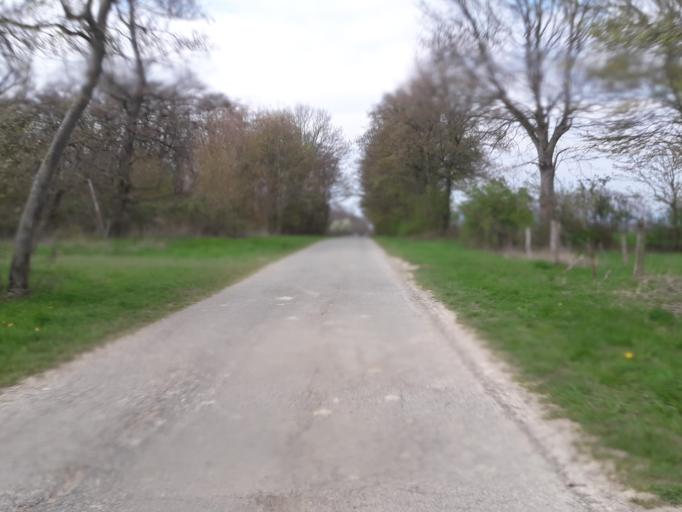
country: DE
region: North Rhine-Westphalia
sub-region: Regierungsbezirk Detmold
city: Paderborn
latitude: 51.6882
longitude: 8.7659
